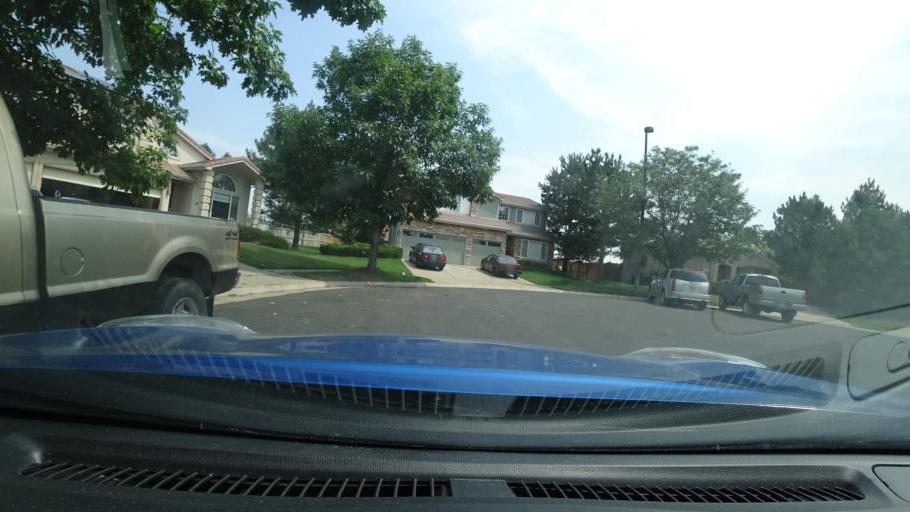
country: US
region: Colorado
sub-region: Adams County
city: Aurora
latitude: 39.7821
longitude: -104.7552
